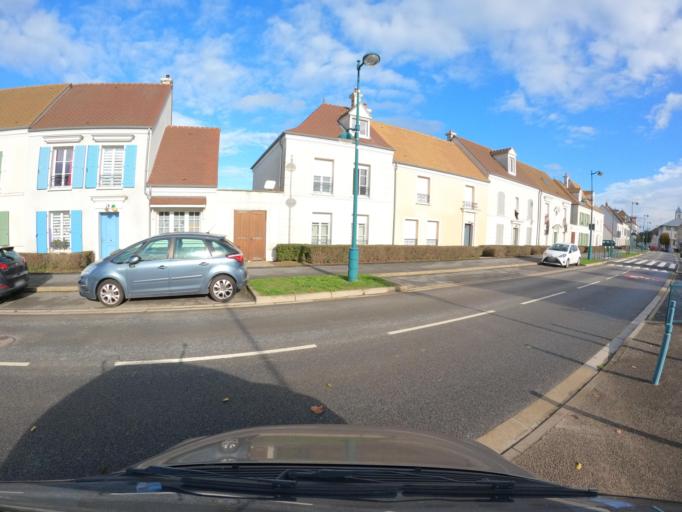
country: FR
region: Ile-de-France
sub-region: Departement de Seine-et-Marne
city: Bailly-Romainvilliers
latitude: 48.8526
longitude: 2.8264
